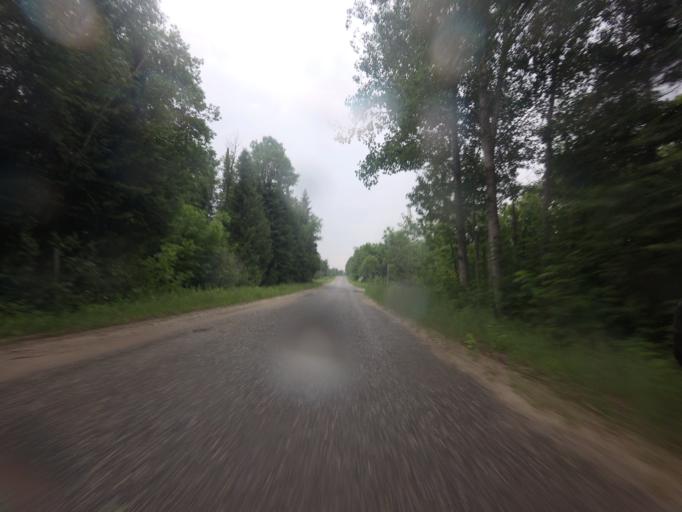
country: CA
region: Quebec
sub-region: Outaouais
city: Maniwaki
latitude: 46.4309
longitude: -75.9482
